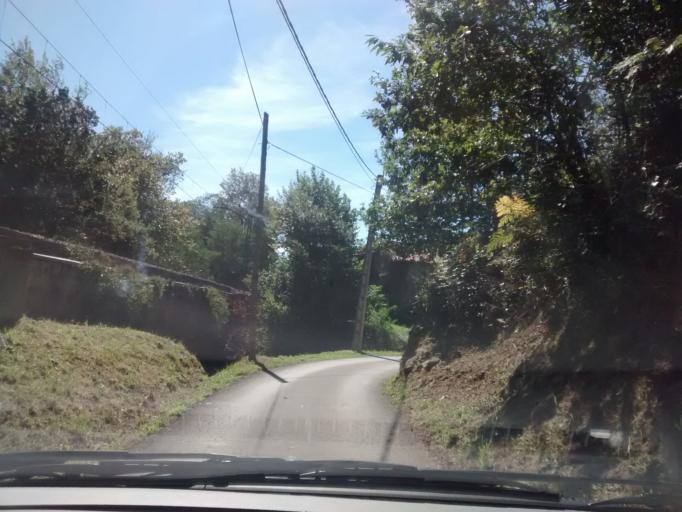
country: ES
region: Cantabria
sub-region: Provincia de Cantabria
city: Entrambasaguas
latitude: 43.3653
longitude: -3.7141
